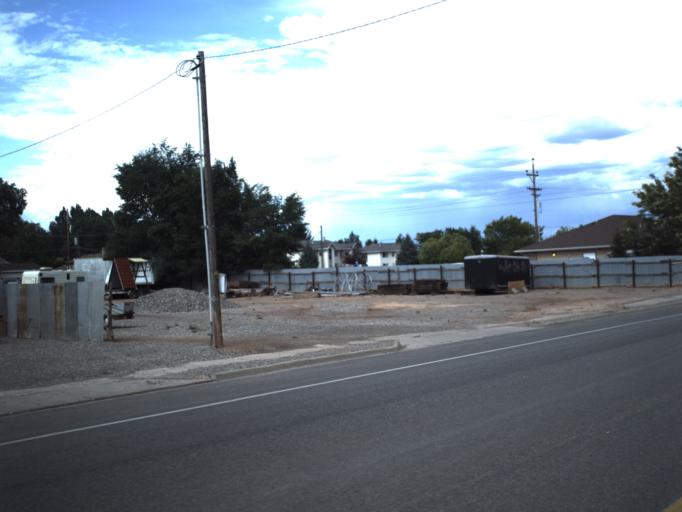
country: US
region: Utah
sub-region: Sevier County
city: Richfield
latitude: 38.7722
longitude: -112.0755
